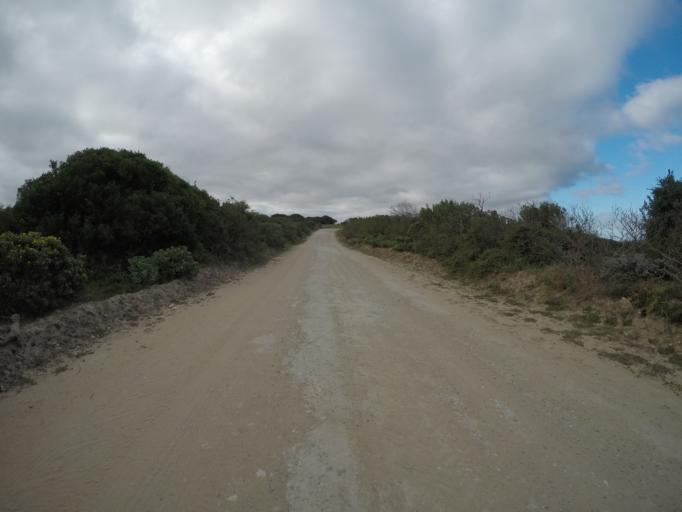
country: ZA
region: Western Cape
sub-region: Eden District Municipality
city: Riversdale
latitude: -34.4228
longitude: 21.3306
